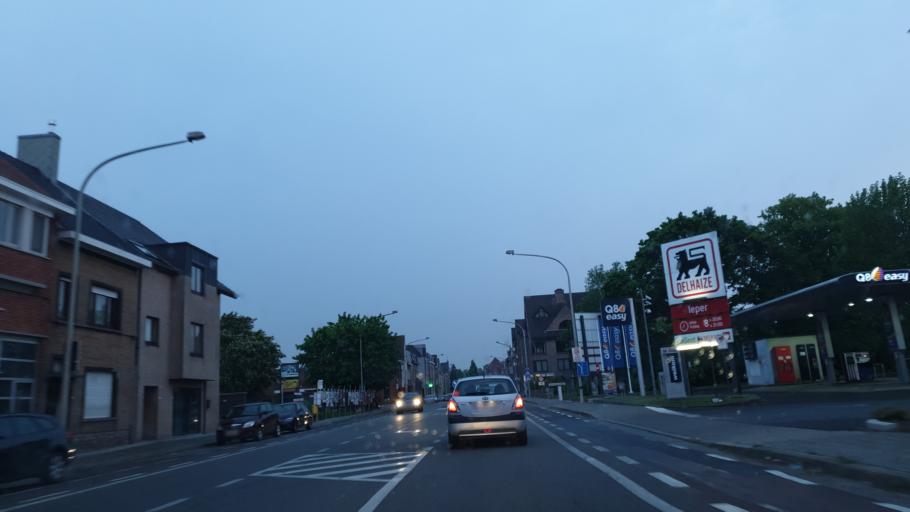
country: BE
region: Flanders
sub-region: Provincie West-Vlaanderen
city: Ieper
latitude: 50.8534
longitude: 2.8747
